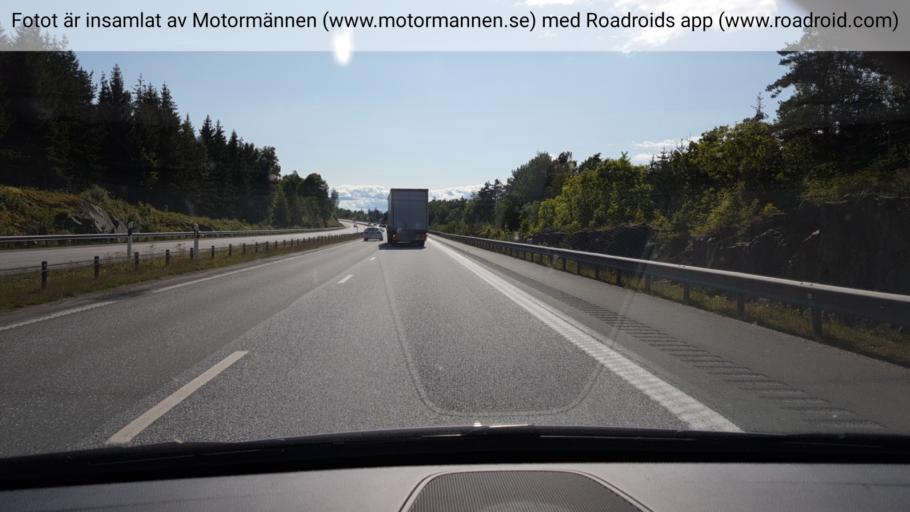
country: SE
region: Joenkoeping
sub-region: Jonkopings Kommun
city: Kaxholmen
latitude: 57.9645
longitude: 14.3601
